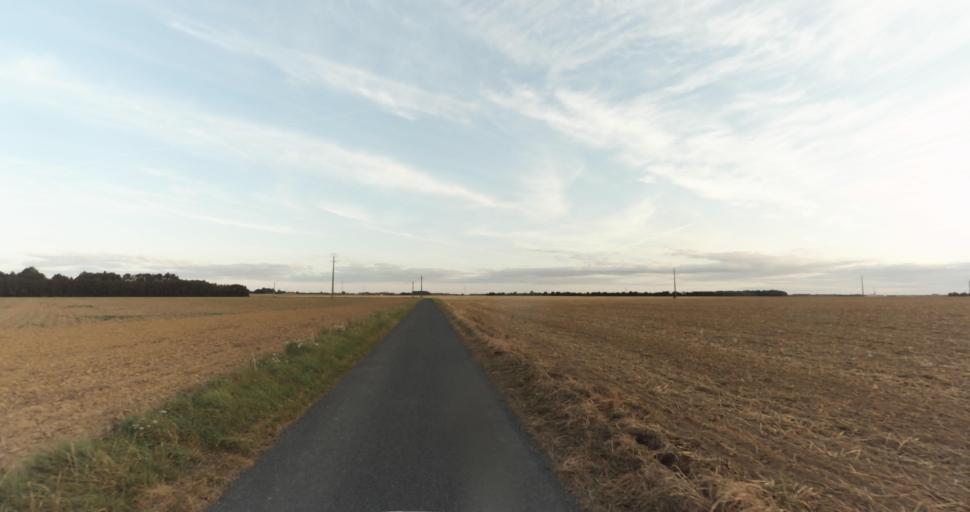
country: FR
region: Haute-Normandie
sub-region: Departement de l'Eure
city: La Madeleine-de-Nonancourt
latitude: 48.8796
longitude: 1.2283
